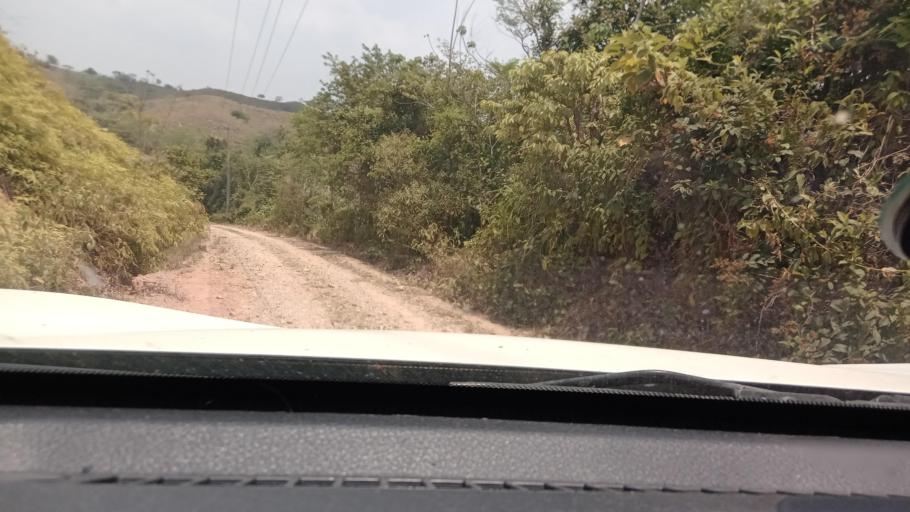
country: MX
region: Tabasco
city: Chontalpa
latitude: 17.5571
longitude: -93.7291
